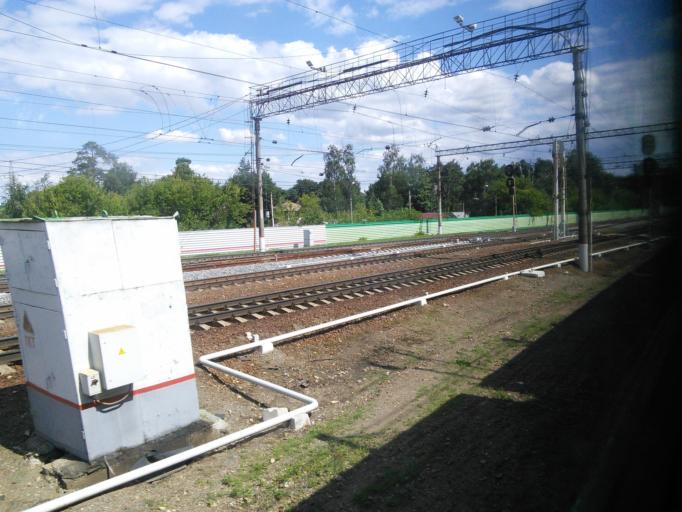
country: RU
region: Moskovskaya
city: Tomilino
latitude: 55.6598
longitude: 37.9411
